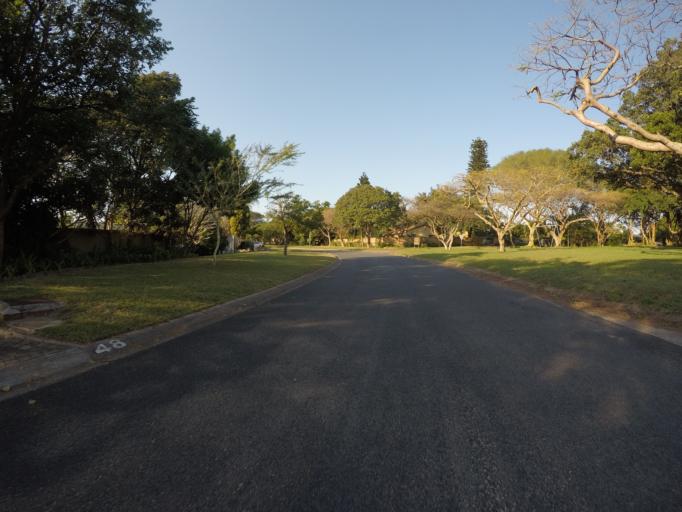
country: ZA
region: KwaZulu-Natal
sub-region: uThungulu District Municipality
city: Richards Bay
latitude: -28.7738
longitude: 32.1060
